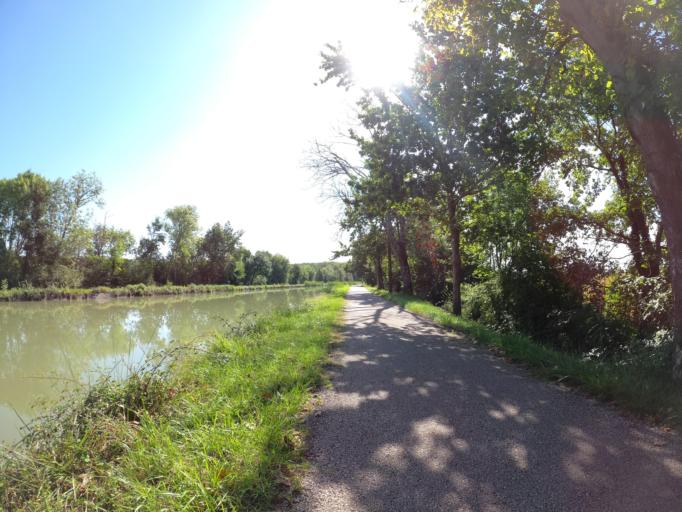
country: FR
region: Midi-Pyrenees
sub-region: Departement du Tarn-et-Garonne
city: Montech
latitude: 43.9474
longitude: 1.2524
